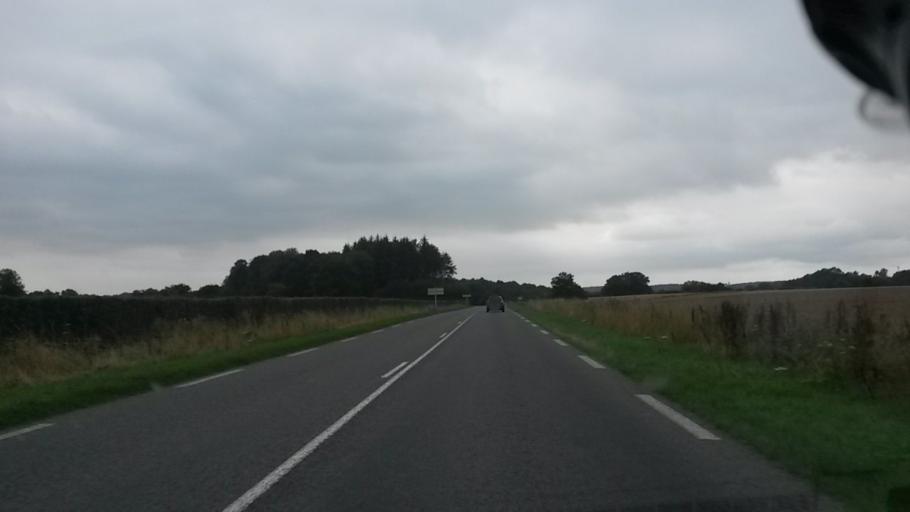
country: FR
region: Haute-Normandie
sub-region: Departement de la Seine-Maritime
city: Aumale
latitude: 49.7657
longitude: 1.7862
